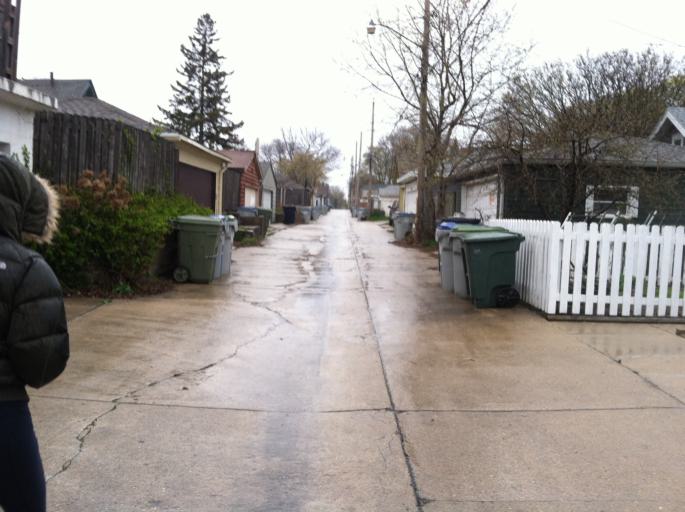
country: US
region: Wisconsin
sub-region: Milwaukee County
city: Shorewood
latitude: 43.0731
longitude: -87.8897
